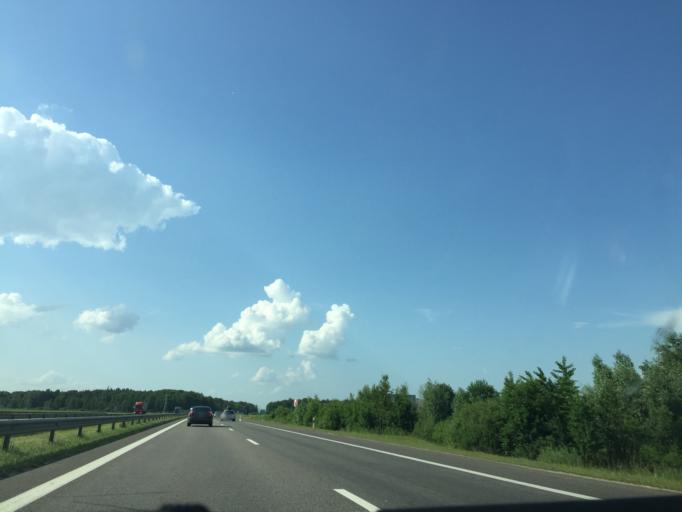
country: LT
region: Kauno apskritis
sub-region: Kaunas
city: Sargenai
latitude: 54.9702
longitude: 23.8571
